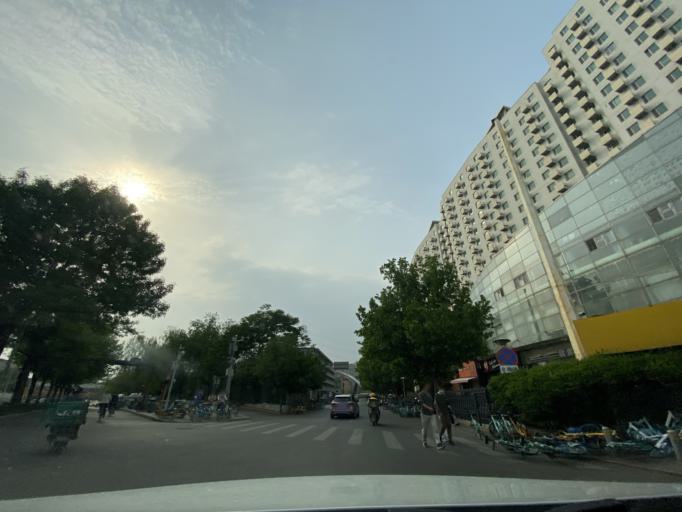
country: CN
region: Beijing
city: Haidian
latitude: 39.9752
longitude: 116.3373
